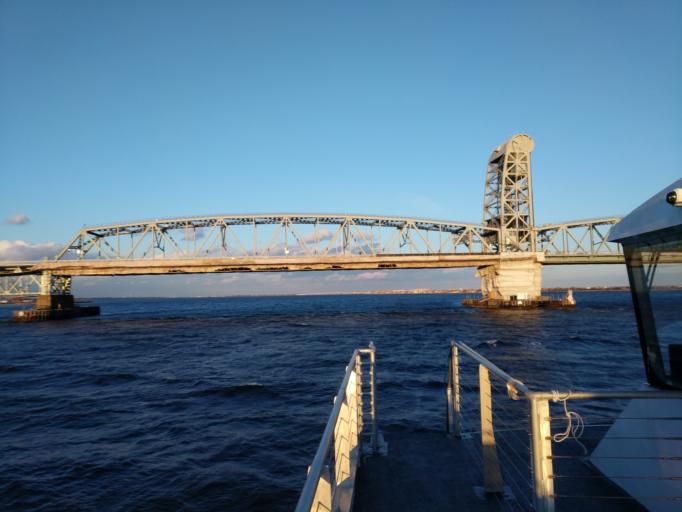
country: US
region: New York
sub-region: Kings County
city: East New York
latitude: 40.5743
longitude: -73.8880
